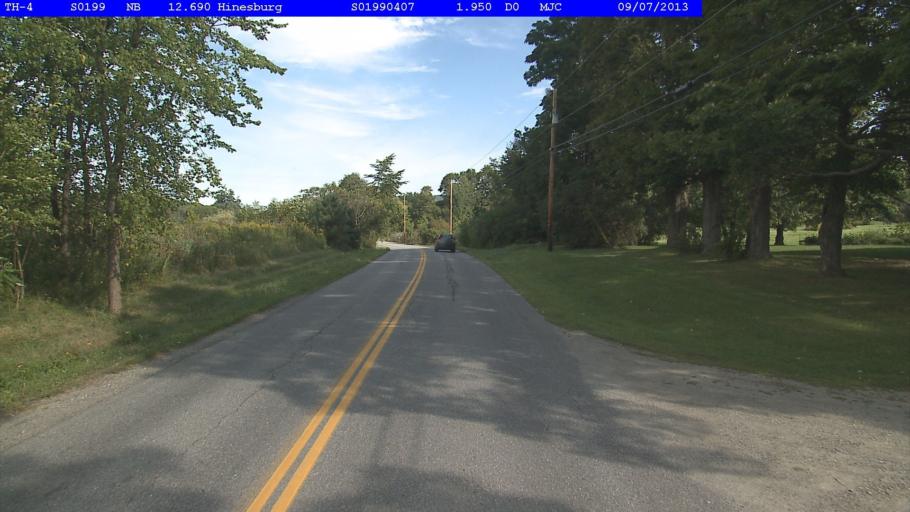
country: US
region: Vermont
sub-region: Chittenden County
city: Hinesburg
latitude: 44.3060
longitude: -73.1087
